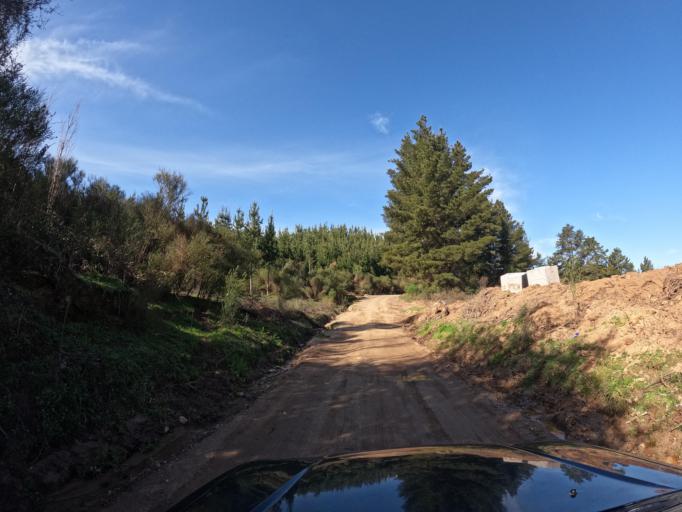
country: CL
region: Biobio
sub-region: Provincia de Biobio
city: La Laja
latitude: -37.0878
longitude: -72.7752
